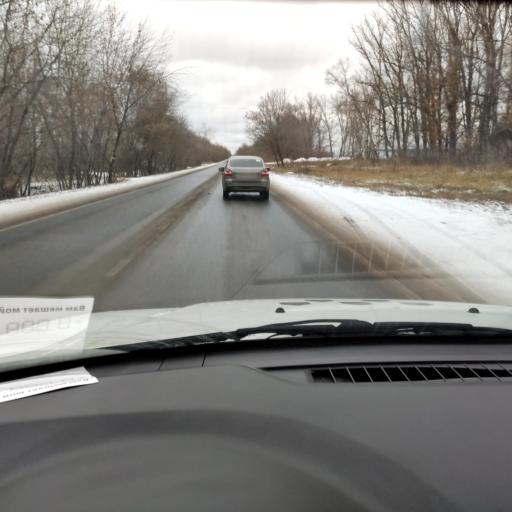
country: RU
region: Samara
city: Tol'yatti
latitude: 53.5519
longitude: 49.3937
